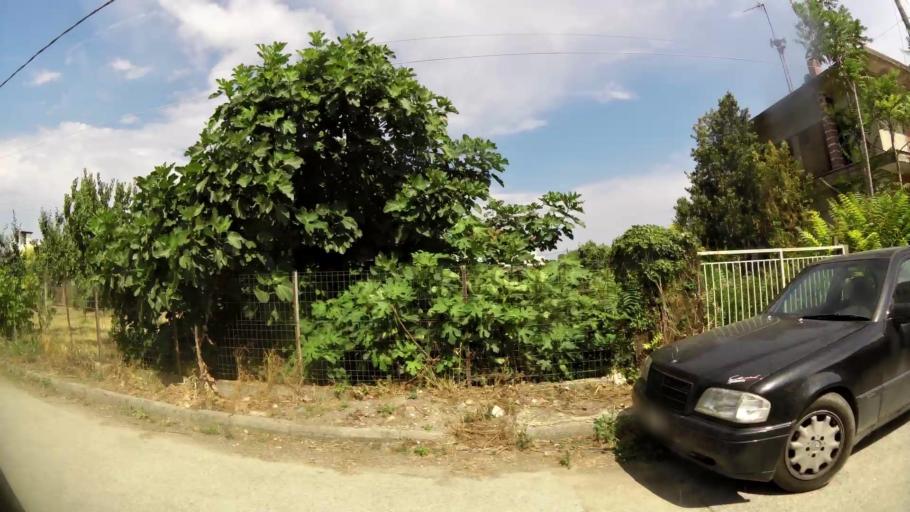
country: GR
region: Central Macedonia
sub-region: Nomos Pierias
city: Korinos
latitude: 40.3137
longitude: 22.5931
